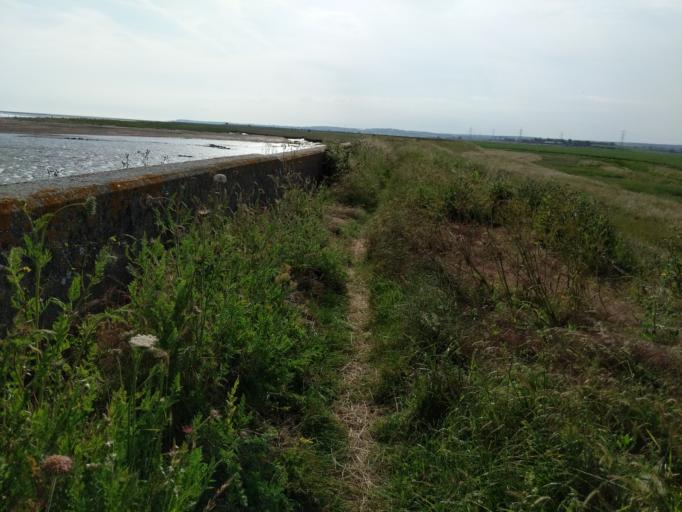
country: GB
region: England
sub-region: Kent
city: Faversham
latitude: 51.3437
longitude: 0.9117
